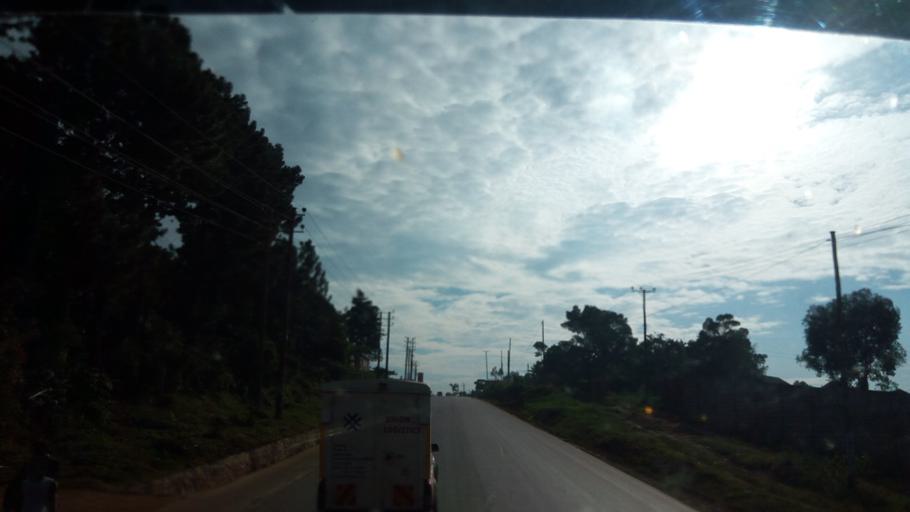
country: UG
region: Central Region
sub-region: Wakiso District
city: Wakiso
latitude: 0.4478
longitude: 32.5297
